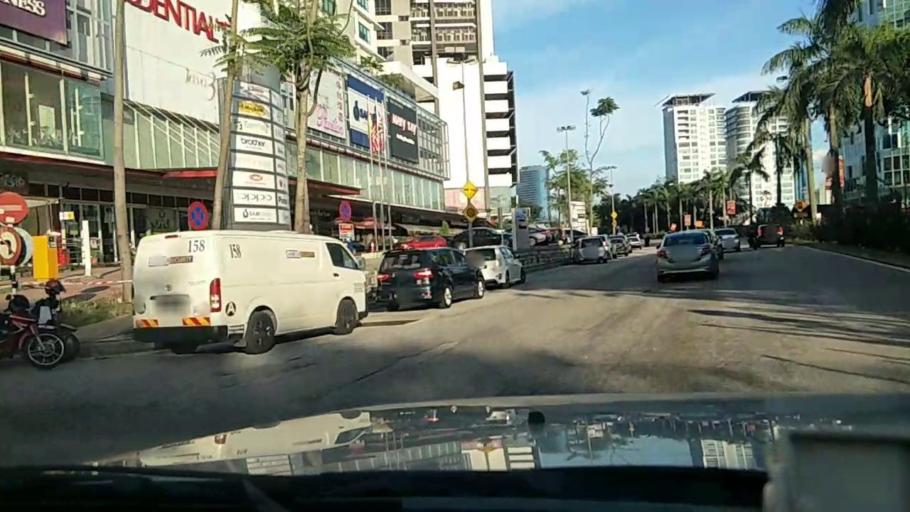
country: MY
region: Selangor
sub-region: Petaling
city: Petaling Jaya
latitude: 3.1105
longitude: 101.6367
